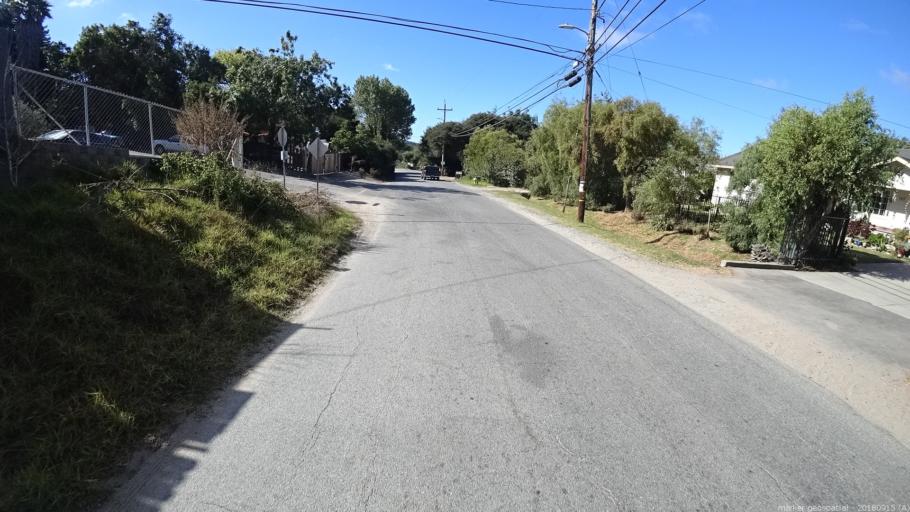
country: US
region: California
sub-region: Monterey County
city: Las Lomas
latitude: 36.8731
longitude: -121.7357
